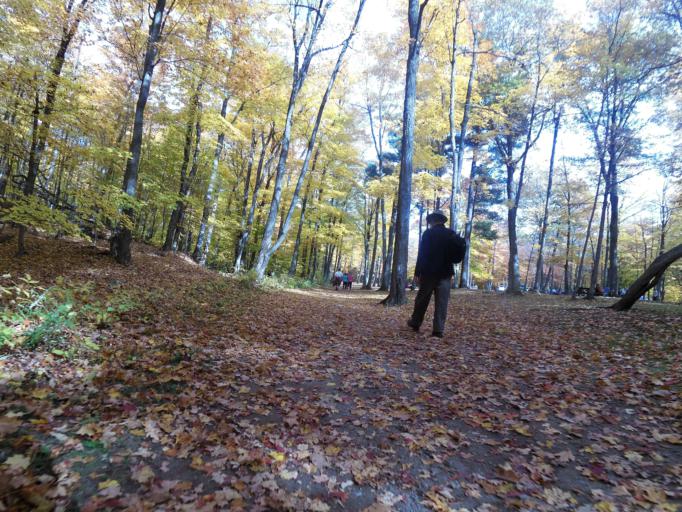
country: CA
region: Quebec
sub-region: Outaouais
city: Gatineau
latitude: 45.4994
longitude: -75.8326
